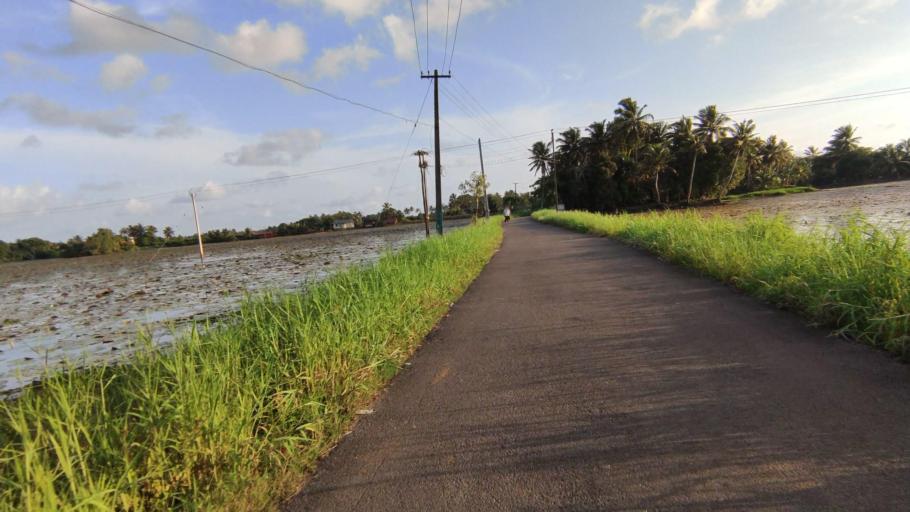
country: IN
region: Kerala
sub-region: Kottayam
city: Kottayam
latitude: 9.5912
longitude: 76.4486
